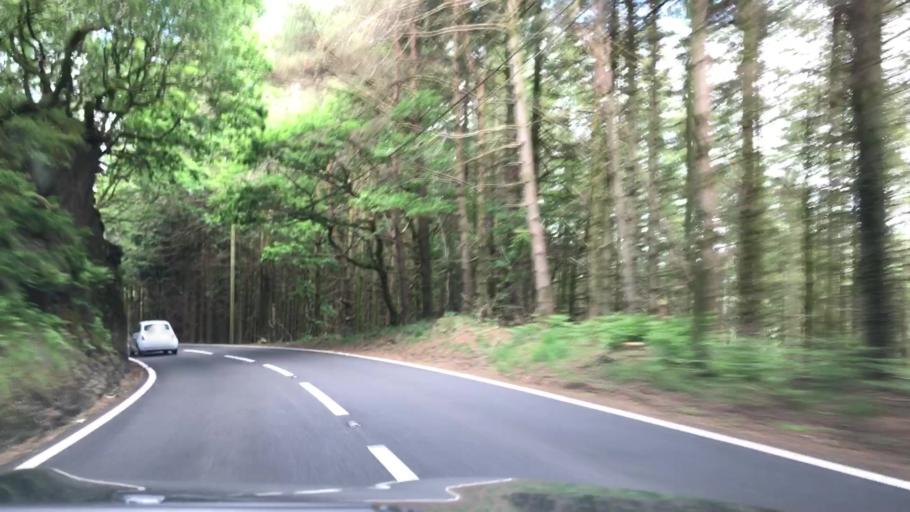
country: GB
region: Wales
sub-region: County of Ceredigion
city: Bow Street
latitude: 52.4126
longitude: -3.9164
